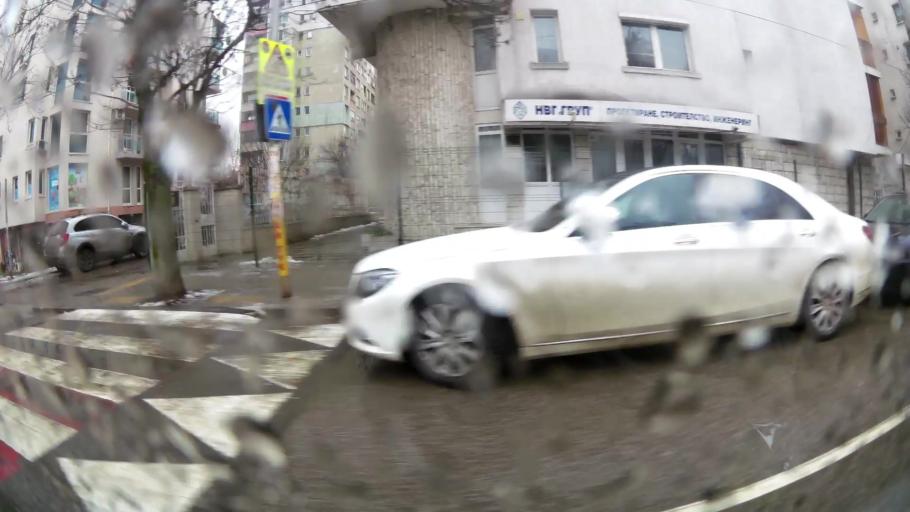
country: BG
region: Sofia-Capital
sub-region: Stolichna Obshtina
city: Sofia
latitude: 42.6651
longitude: 23.2988
